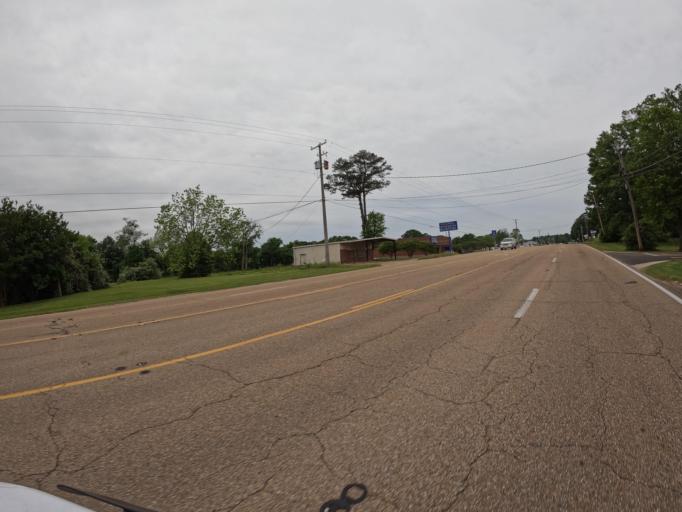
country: US
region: Mississippi
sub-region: Lee County
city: Tupelo
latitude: 34.2875
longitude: -88.7426
